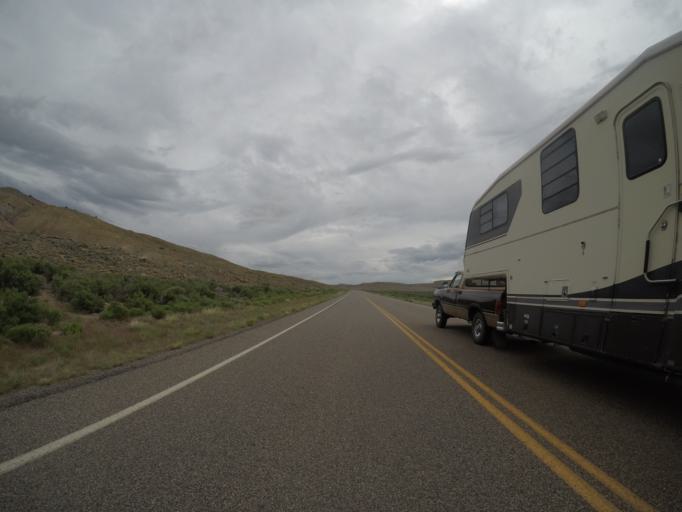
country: US
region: Wyoming
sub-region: Big Horn County
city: Lovell
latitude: 44.9573
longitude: -108.2905
